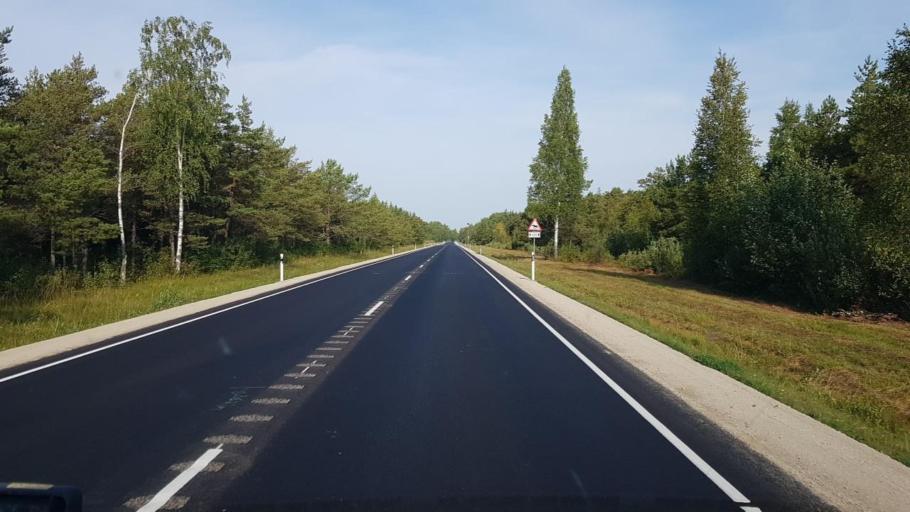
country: EE
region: Saare
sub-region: Orissaare vald
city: Orissaare
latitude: 58.5783
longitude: 23.3650
